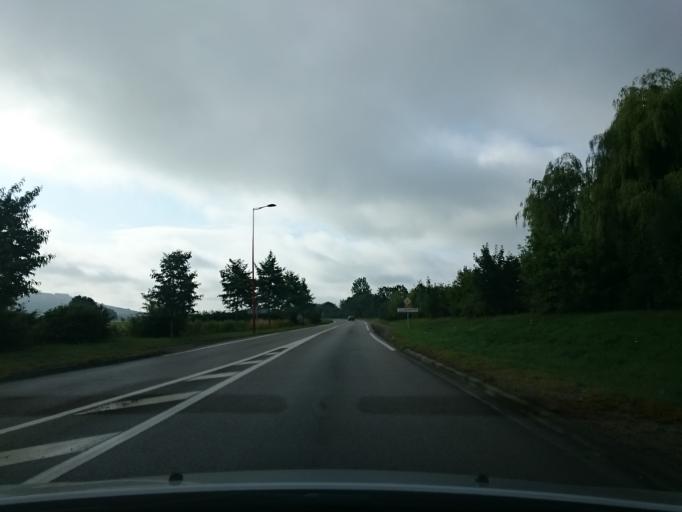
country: FR
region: Lower Normandy
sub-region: Departement du Calvados
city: Cambremer
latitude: 49.1401
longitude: -0.0085
